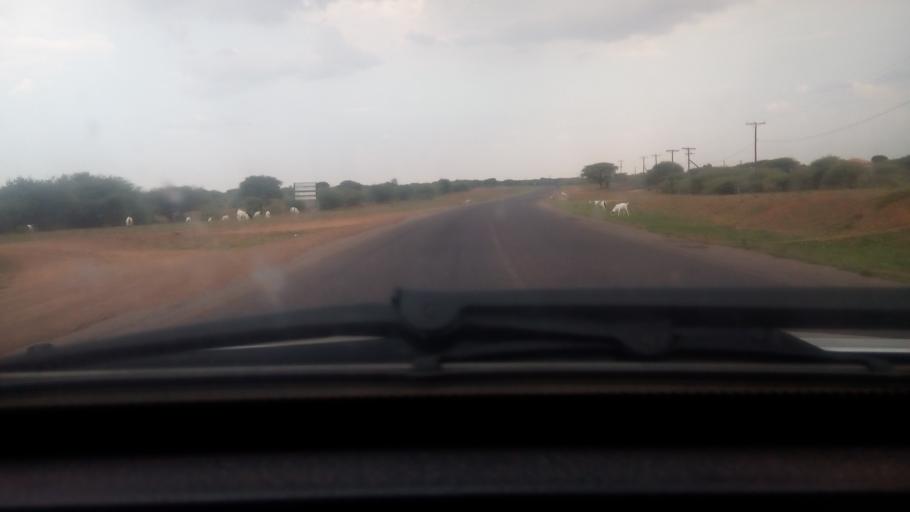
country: BW
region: Kweneng
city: Metsemotlhaba
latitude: -24.4655
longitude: 25.6717
